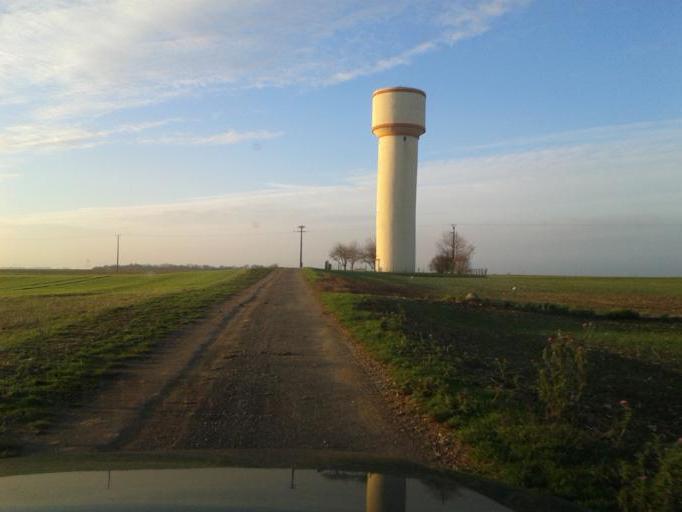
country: FR
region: Centre
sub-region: Departement du Loiret
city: Tavers
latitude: 47.7673
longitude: 1.6004
